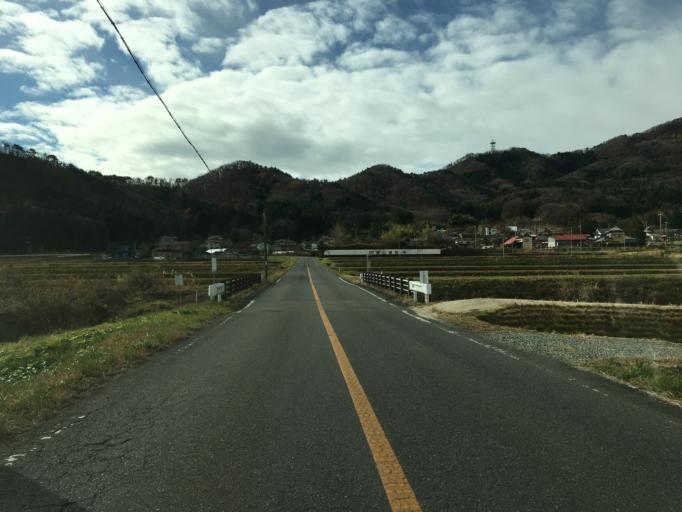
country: JP
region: Fukushima
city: Motomiya
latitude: 37.5214
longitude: 140.3706
